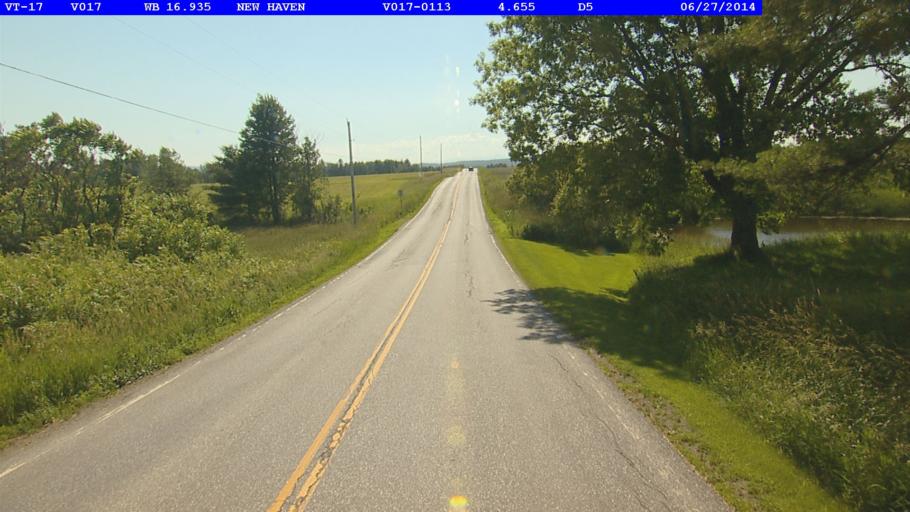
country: US
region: Vermont
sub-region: Addison County
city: Bristol
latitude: 44.1240
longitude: -73.1579
